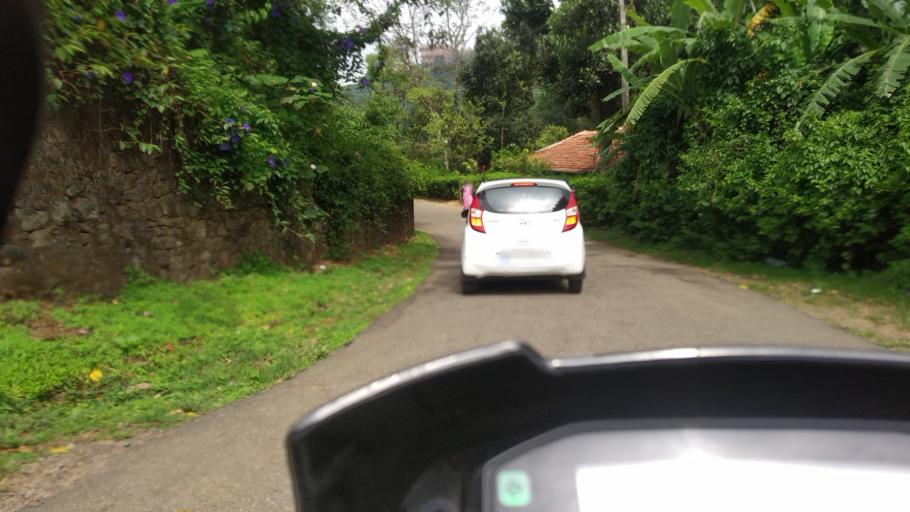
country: IN
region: Tamil Nadu
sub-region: Theni
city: Gudalur
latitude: 9.5787
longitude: 77.0146
